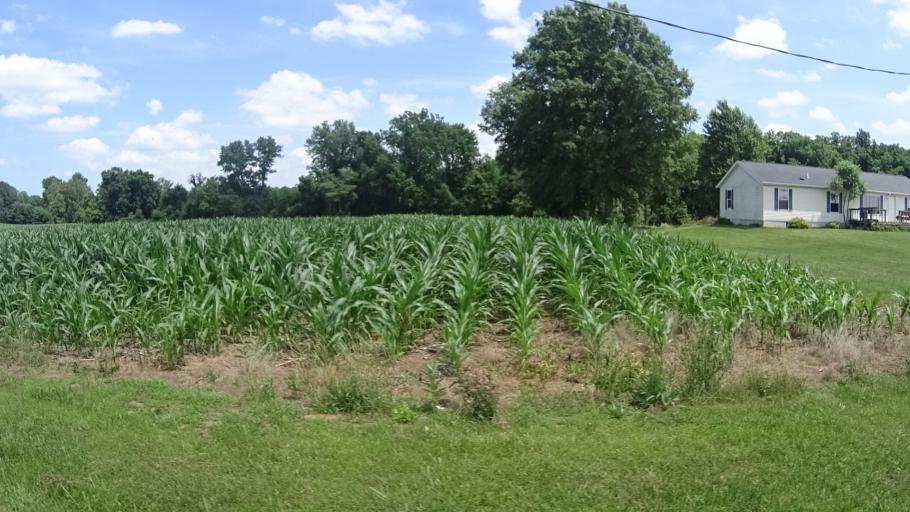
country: US
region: Ohio
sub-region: Erie County
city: Milan
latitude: 41.3116
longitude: -82.5355
